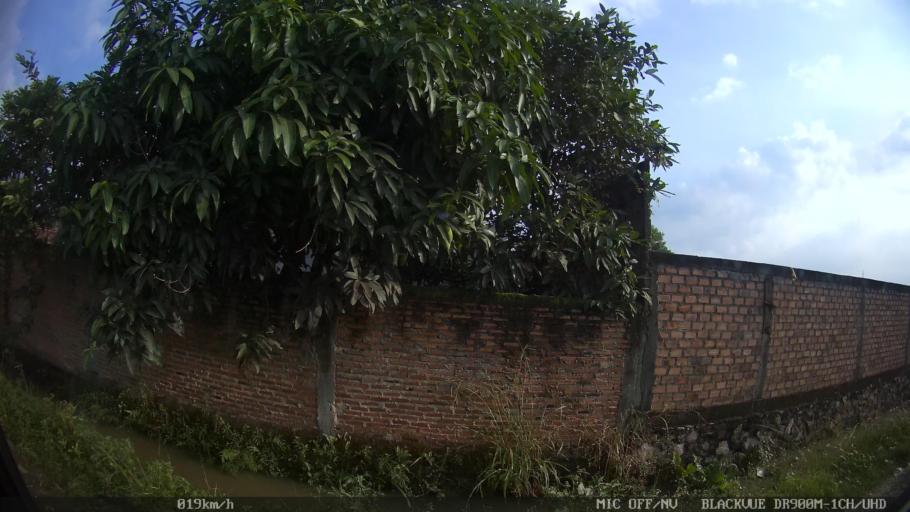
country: ID
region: Lampung
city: Kedaton
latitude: -5.3911
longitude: 105.3128
